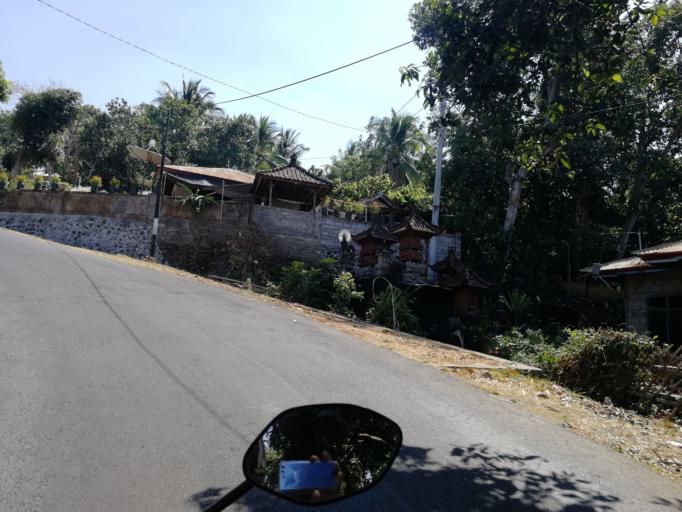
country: ID
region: Bali
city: Banjar Kedisan
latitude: -8.1423
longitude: 115.3152
